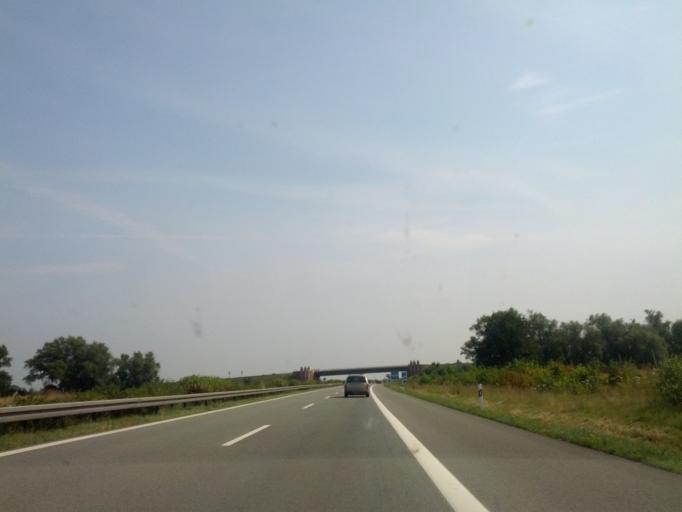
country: DE
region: Mecklenburg-Vorpommern
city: Grimmen
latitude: 54.0876
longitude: 13.1228
